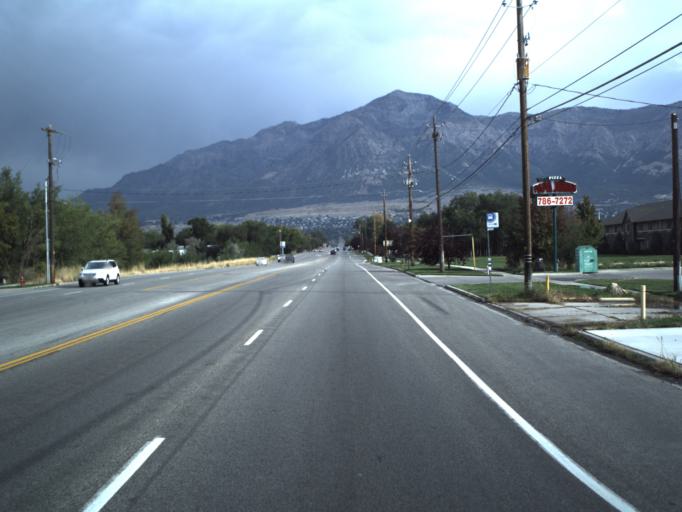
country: US
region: Utah
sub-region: Weber County
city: Harrisville
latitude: 41.2800
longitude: -111.9692
